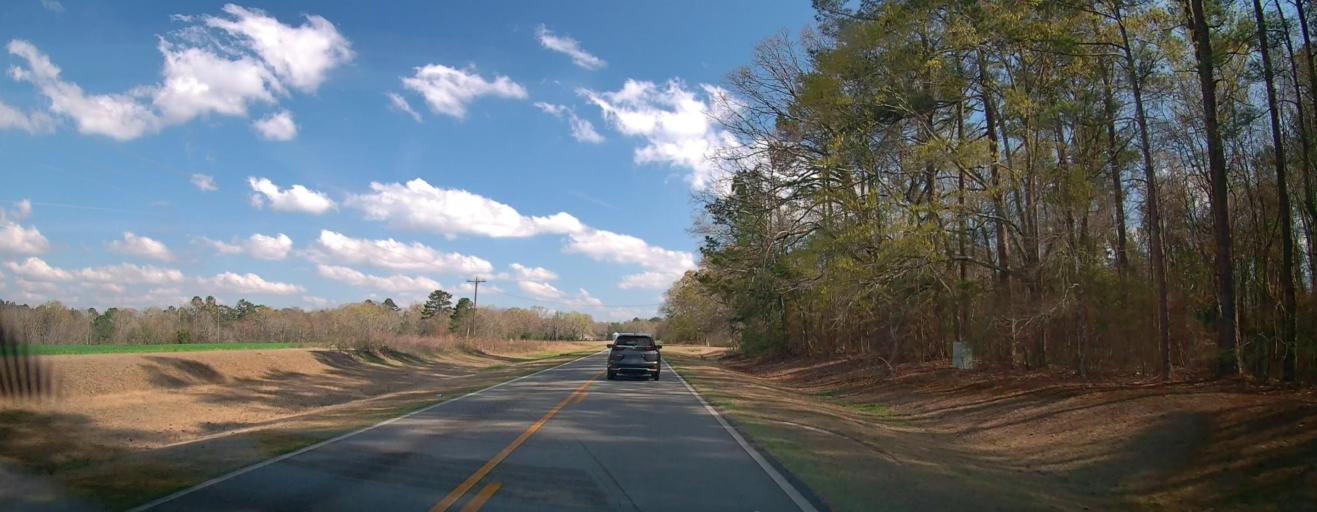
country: US
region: Georgia
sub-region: Wilkinson County
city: Irwinton
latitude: 32.6293
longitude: -83.0982
